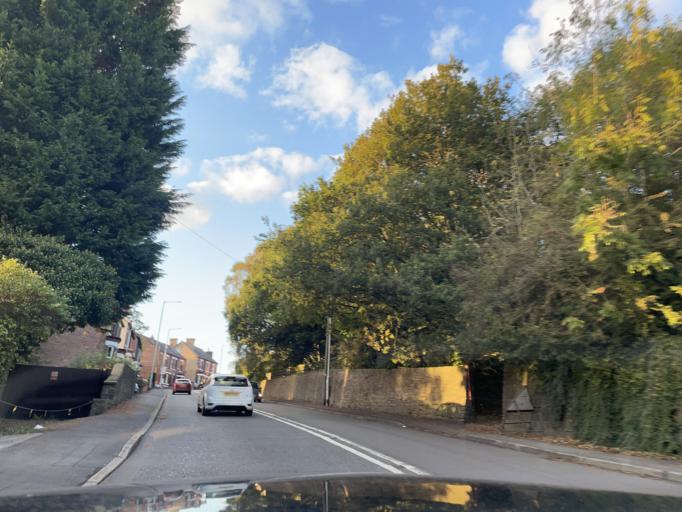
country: GB
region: England
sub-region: Borough of Stockport
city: Marple
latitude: 53.4050
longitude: -2.0513
